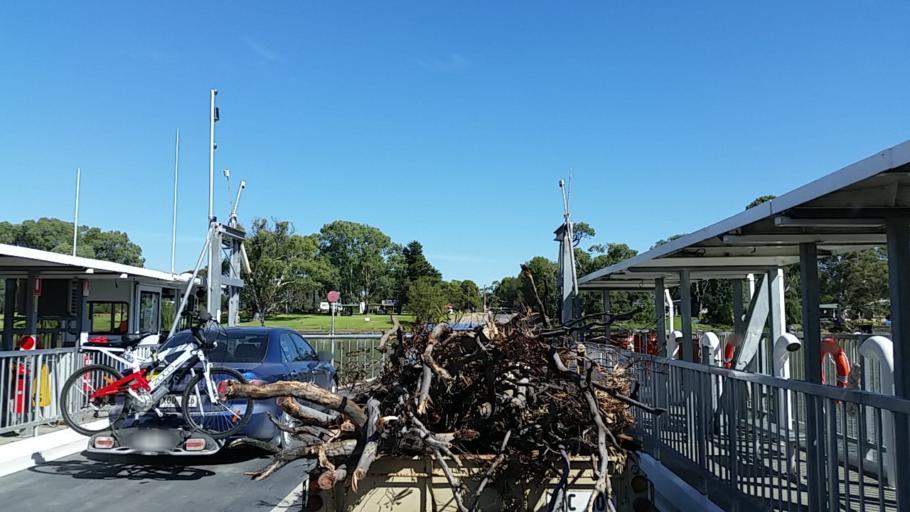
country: AU
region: South Australia
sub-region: Mid Murray
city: Mannum
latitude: -34.7534
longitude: 139.5693
